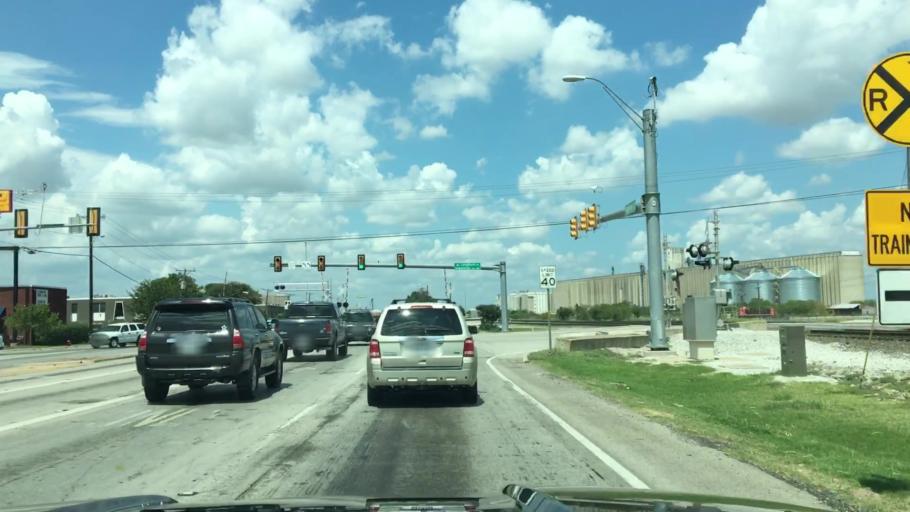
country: US
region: Texas
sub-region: Tarrant County
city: Saginaw
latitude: 32.8474
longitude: -97.3600
